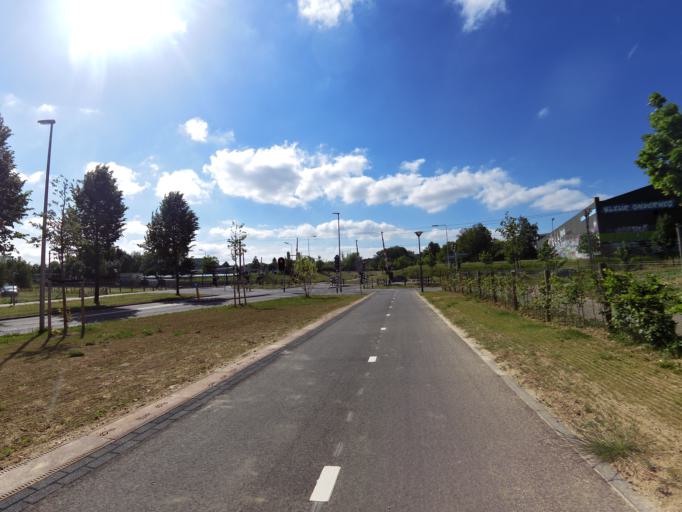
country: NL
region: Limburg
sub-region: Gemeente Heerlen
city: Heerlen
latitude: 50.8905
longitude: 5.9924
